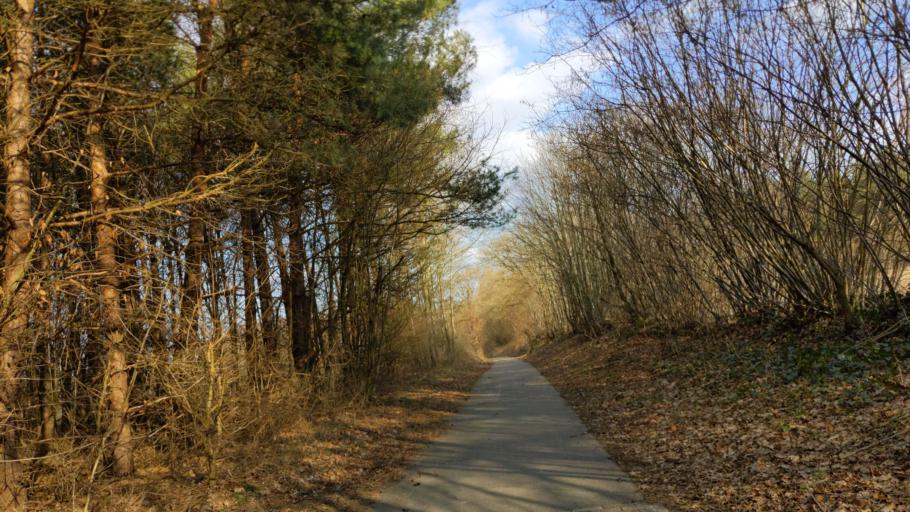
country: DE
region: Schleswig-Holstein
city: Ratekau
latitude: 53.9875
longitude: 10.6806
